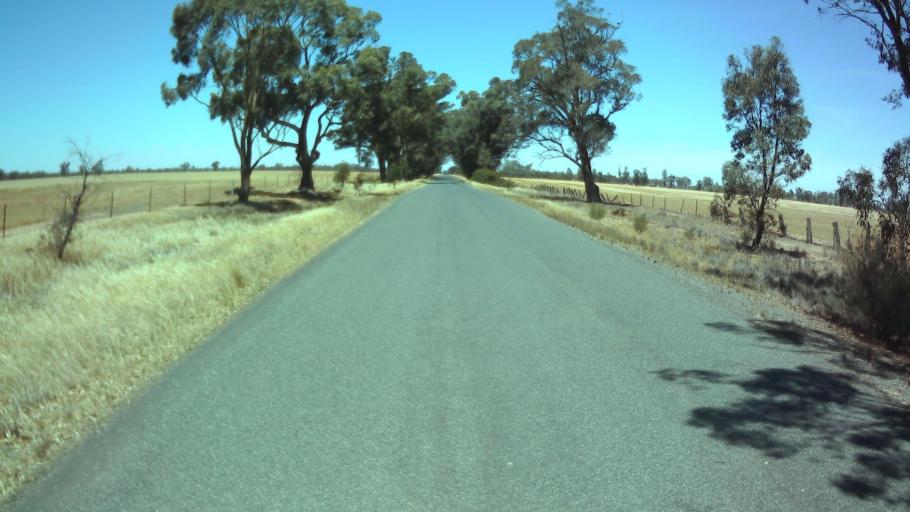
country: AU
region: New South Wales
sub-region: Weddin
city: Grenfell
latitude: -34.0213
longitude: 147.7925
